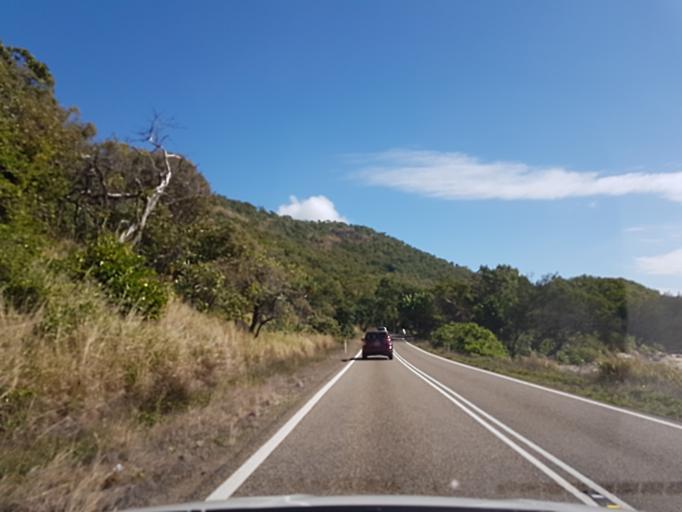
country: AU
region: Queensland
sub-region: Cairns
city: Port Douglas
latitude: -16.6113
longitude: 145.5309
